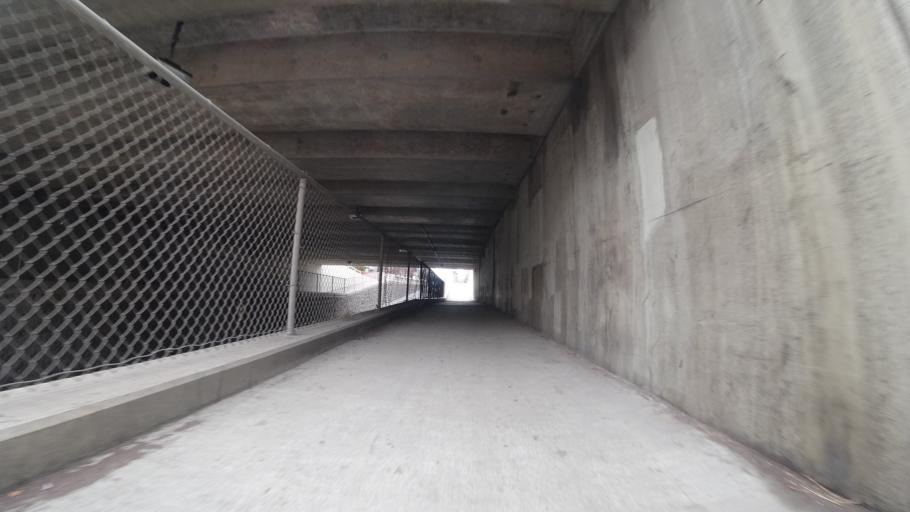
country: US
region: Oregon
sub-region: Deschutes County
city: Bend
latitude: 44.0560
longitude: -121.3070
